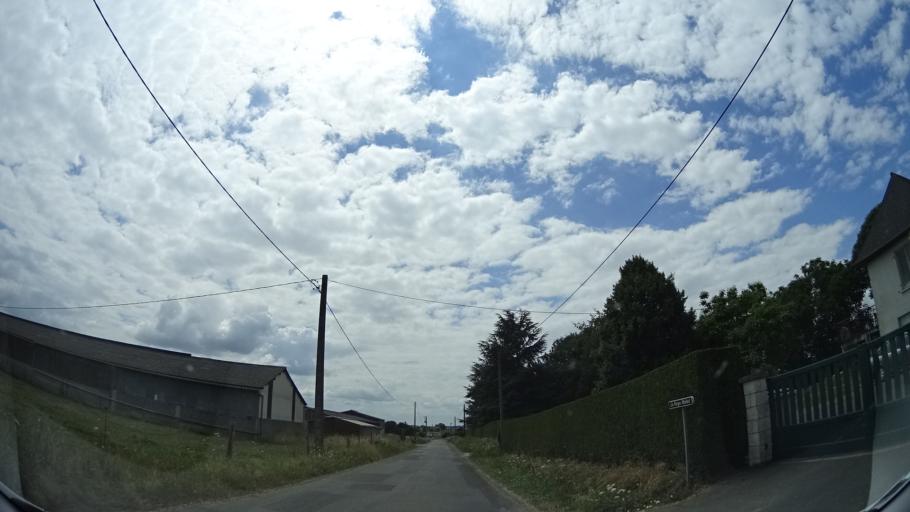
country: FR
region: Brittany
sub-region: Departement d'Ille-et-Vilaine
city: La Chapelle-des-Fougeretz
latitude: 48.1727
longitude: -1.7534
